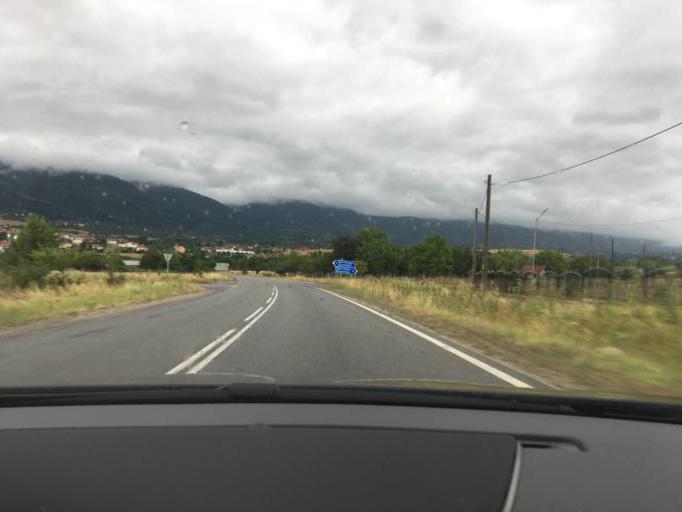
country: BG
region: Kyustendil
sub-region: Obshtina Kyustendil
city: Kyustendil
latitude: 42.2811
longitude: 22.6578
